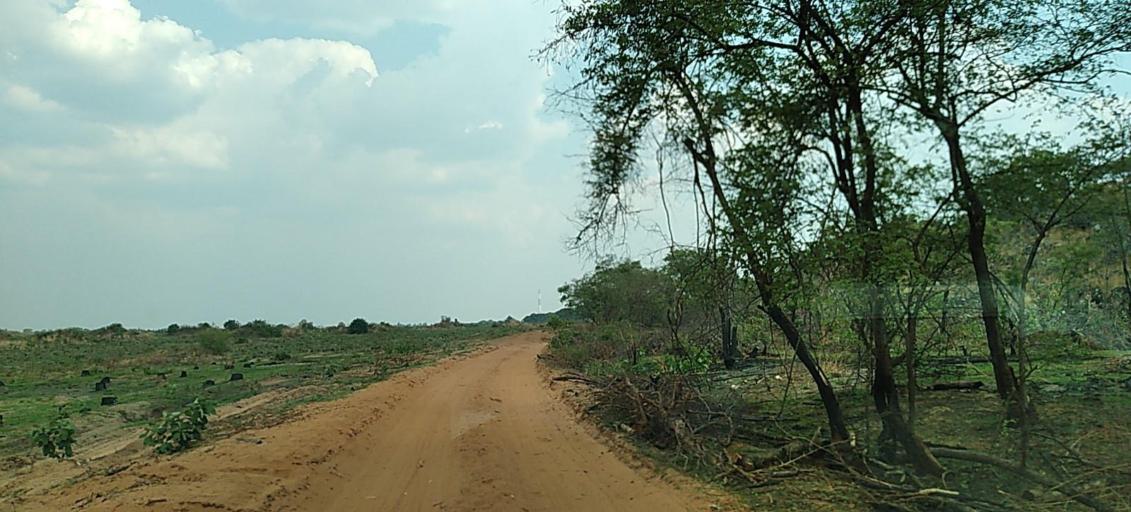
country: ZM
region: Copperbelt
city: Chingola
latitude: -12.7423
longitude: 27.7764
